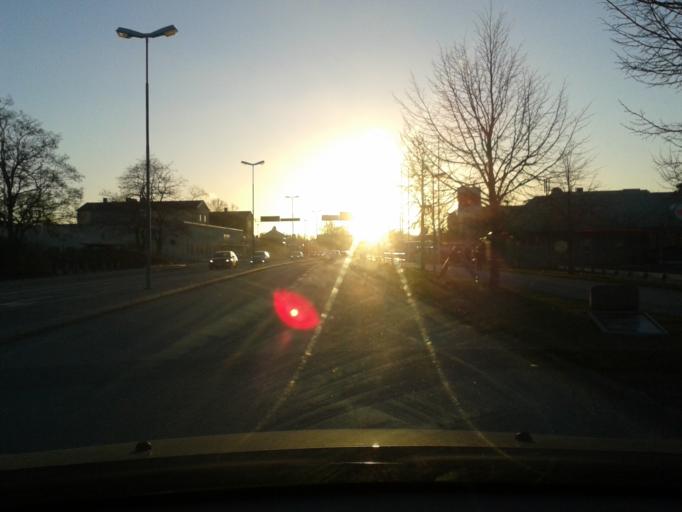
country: SE
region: Gotland
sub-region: Gotland
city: Visby
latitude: 57.6377
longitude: 18.3047
